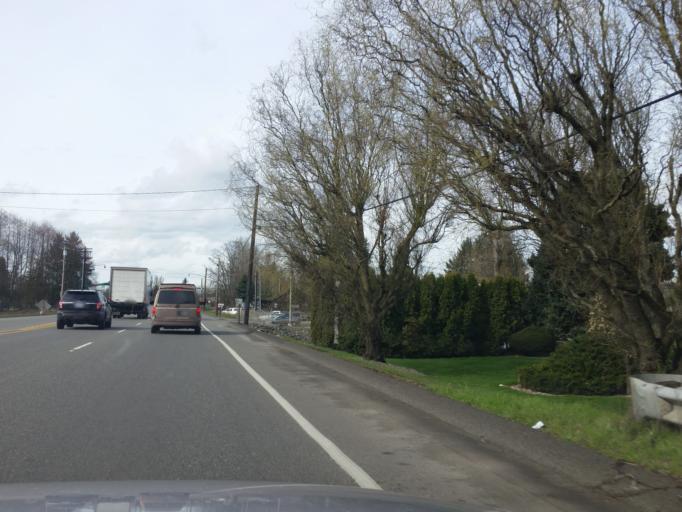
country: US
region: Washington
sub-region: Pierce County
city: Milton
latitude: 47.2197
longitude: -122.3181
